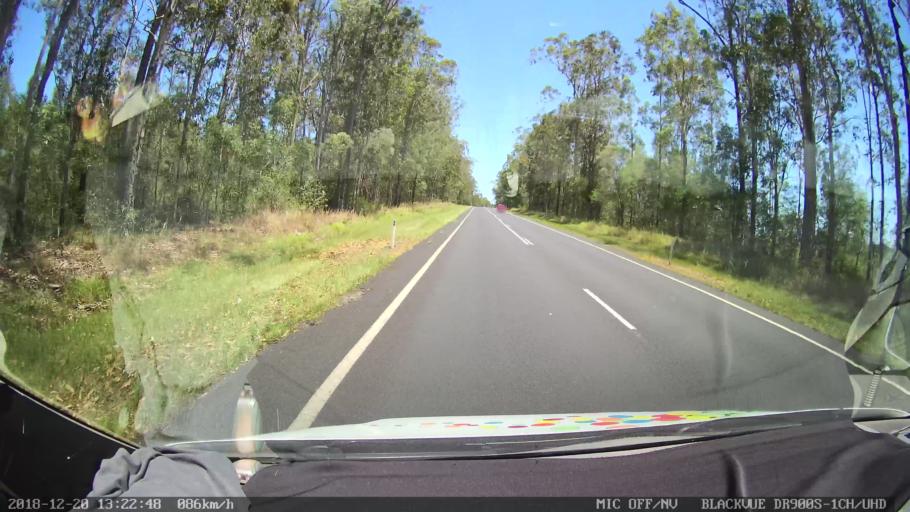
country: AU
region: New South Wales
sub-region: Richmond Valley
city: Casino
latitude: -29.0962
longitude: 153.0012
